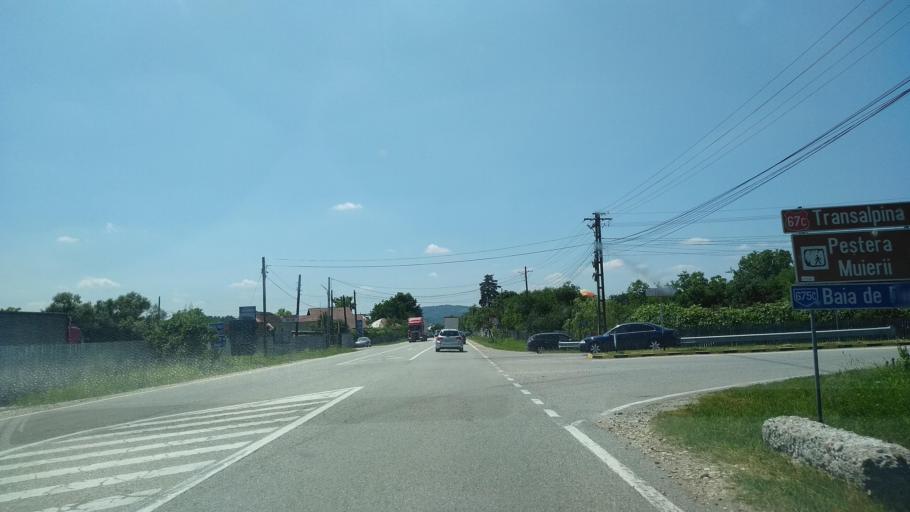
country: RO
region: Gorj
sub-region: Comuna Baia de Fier
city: Baia de Fier
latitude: 45.1377
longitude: 23.7363
